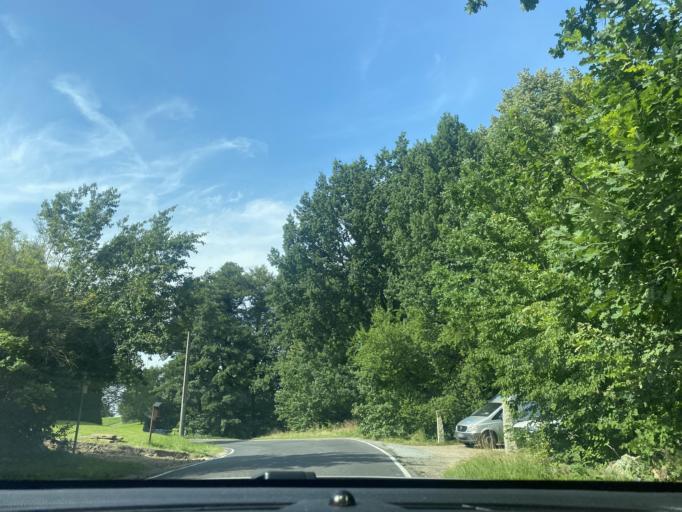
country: DE
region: Saxony
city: Sohland am Rotstein
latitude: 51.1043
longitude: 14.7900
